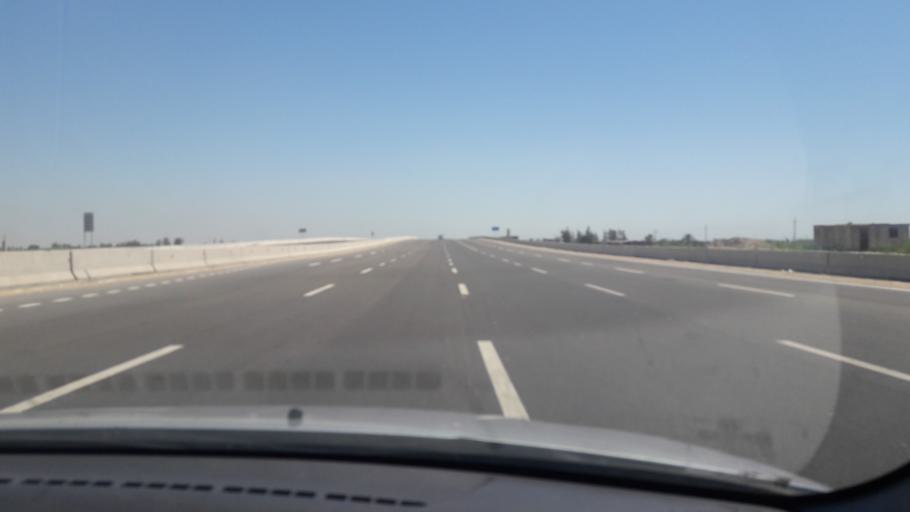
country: EG
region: Muhafazat Bur Sa`id
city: Port Said
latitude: 31.1767
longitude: 32.2354
